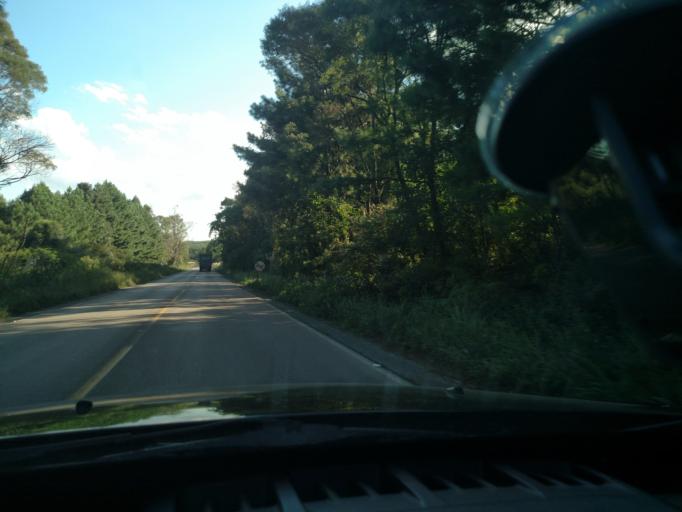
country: BR
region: Santa Catarina
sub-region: Otacilio Costa
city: Otacilio Costa
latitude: -27.3589
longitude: -50.1332
